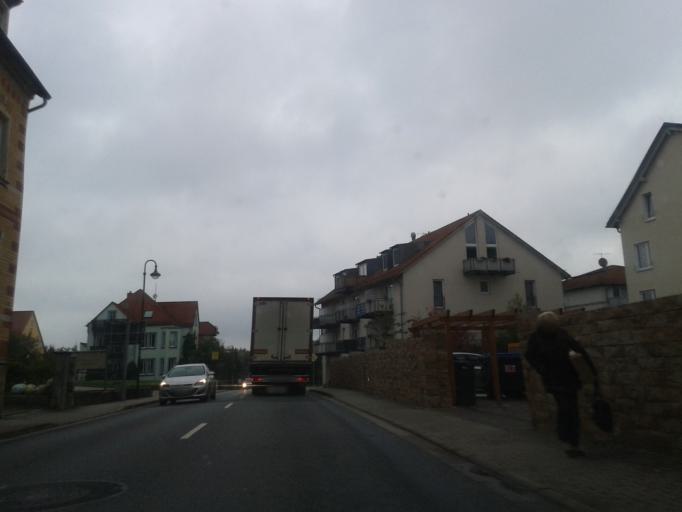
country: DE
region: Saxony
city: Wilsdruff
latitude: 51.0524
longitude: 13.5352
